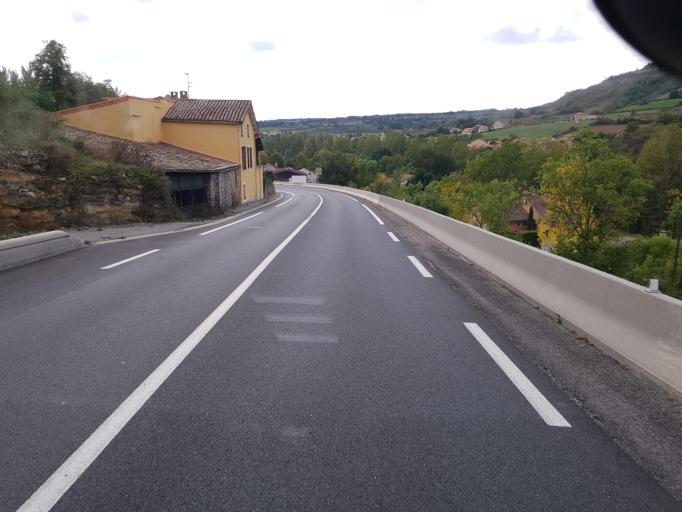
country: FR
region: Midi-Pyrenees
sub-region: Departement de l'Aveyron
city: Saint-Georges-de-Luzencon
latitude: 44.0712
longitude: 2.9874
